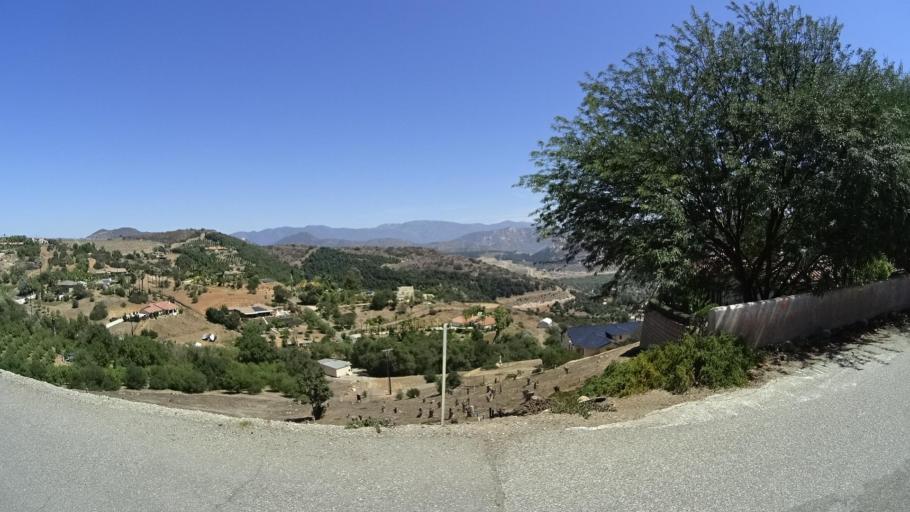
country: US
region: California
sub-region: San Diego County
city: Rainbow
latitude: 33.3485
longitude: -117.1740
